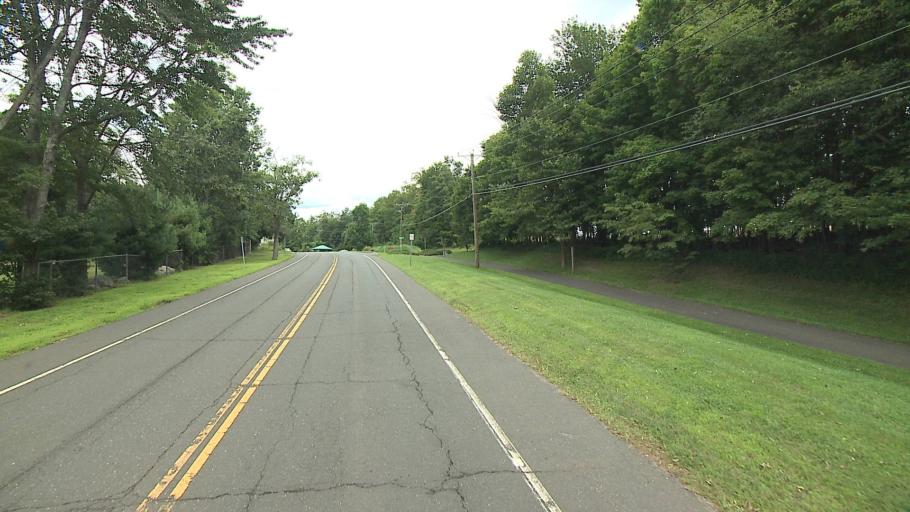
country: US
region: Connecticut
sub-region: New Haven County
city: Middlebury
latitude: 41.5260
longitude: -73.1487
